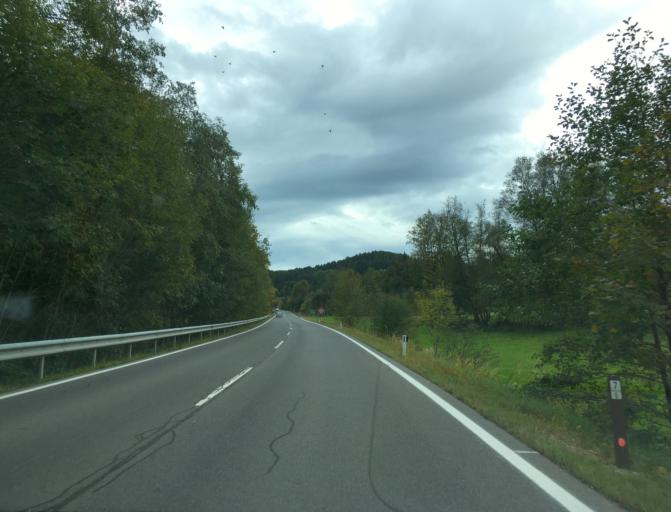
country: AT
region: Lower Austria
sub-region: Politischer Bezirk Neunkirchen
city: Thomasberg
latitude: 47.5515
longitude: 16.1431
